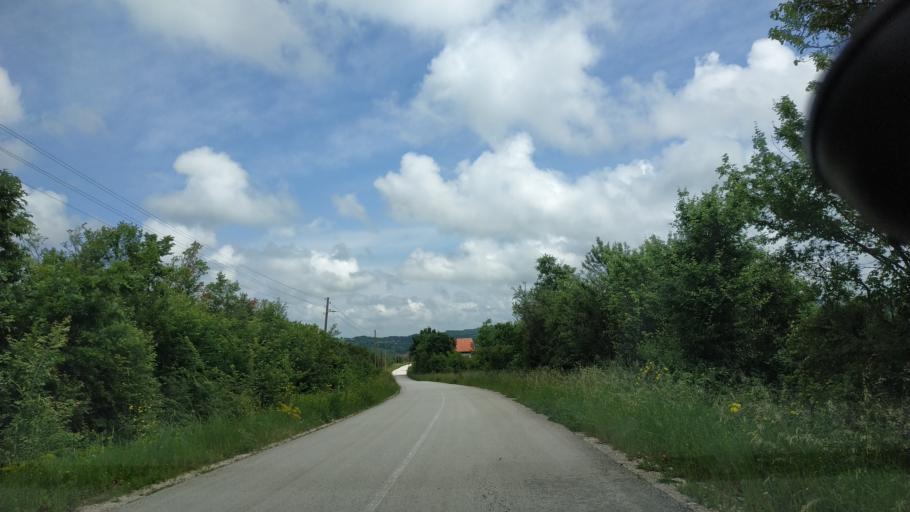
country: RS
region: Central Serbia
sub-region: Zajecarski Okrug
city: Boljevac
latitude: 43.8203
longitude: 21.9537
